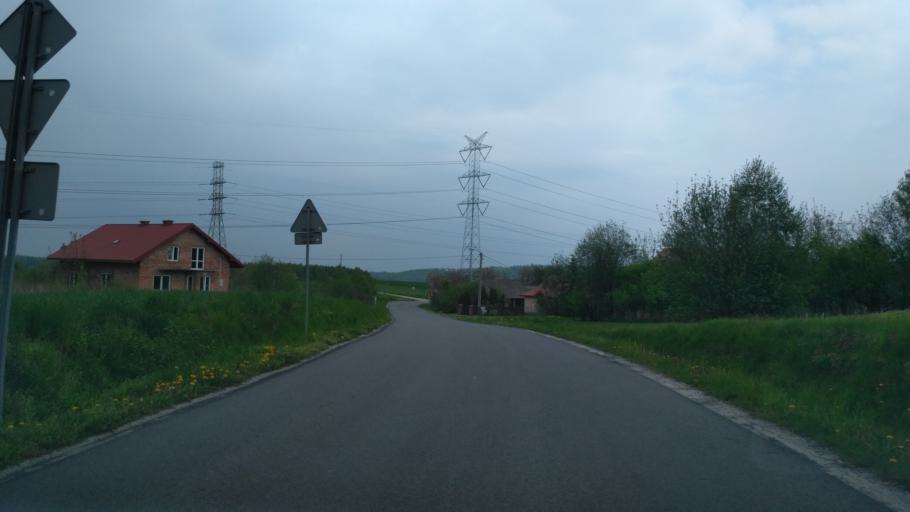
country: PL
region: Lesser Poland Voivodeship
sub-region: Powiat tarnowski
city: Tarnowiec
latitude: 49.9453
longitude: 21.0179
